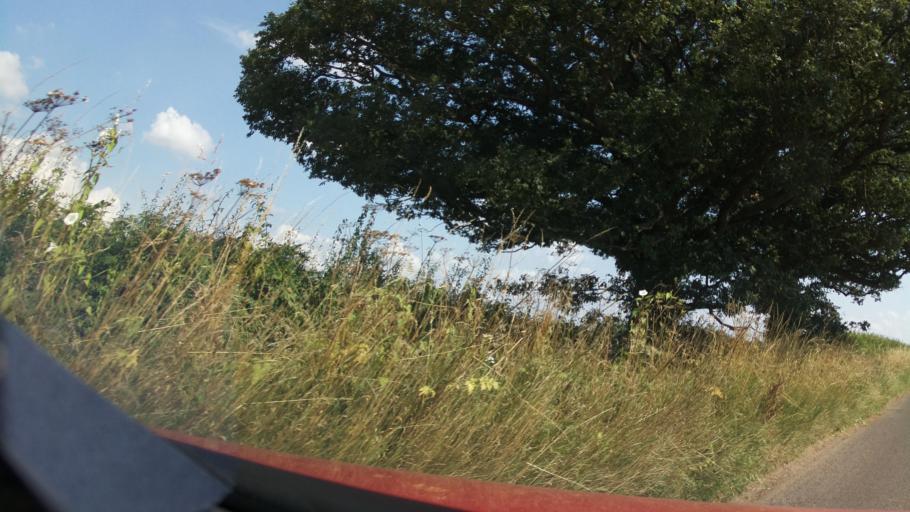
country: GB
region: England
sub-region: Wiltshire
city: Chippenham
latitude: 51.5200
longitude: -2.1077
